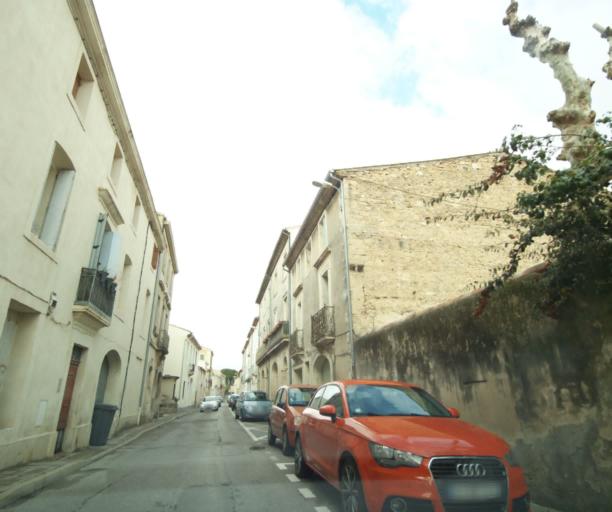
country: FR
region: Languedoc-Roussillon
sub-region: Departement de l'Herault
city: Pignan
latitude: 43.5835
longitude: 3.7648
